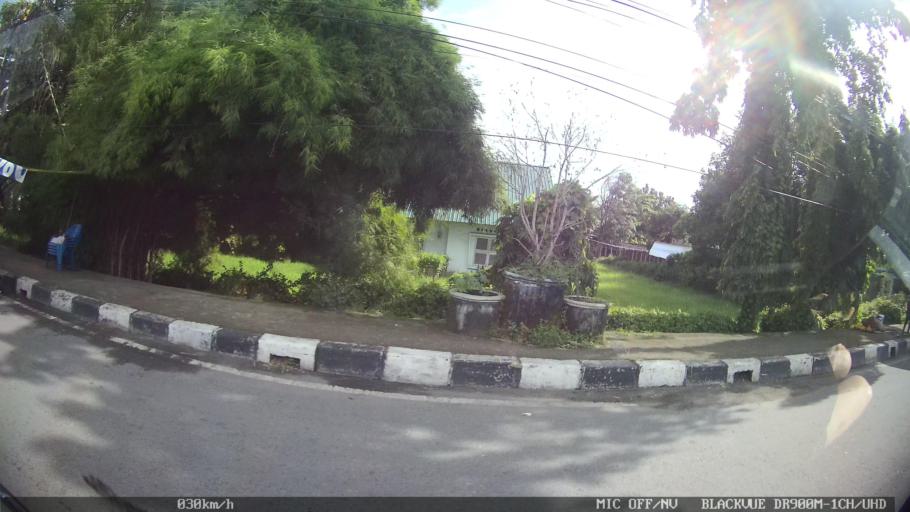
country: ID
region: North Sumatra
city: Medan
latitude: 3.6275
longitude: 98.6637
